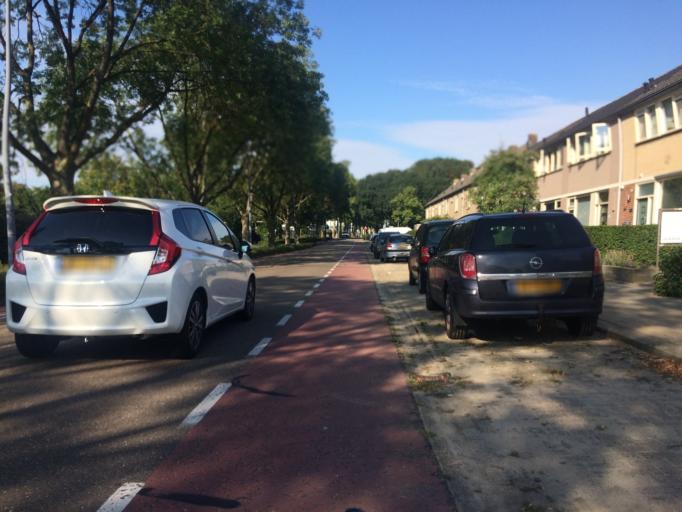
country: NL
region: North Brabant
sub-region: Gemeente 's-Hertogenbosch
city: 's-Hertogenbosch
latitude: 51.7036
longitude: 5.2607
